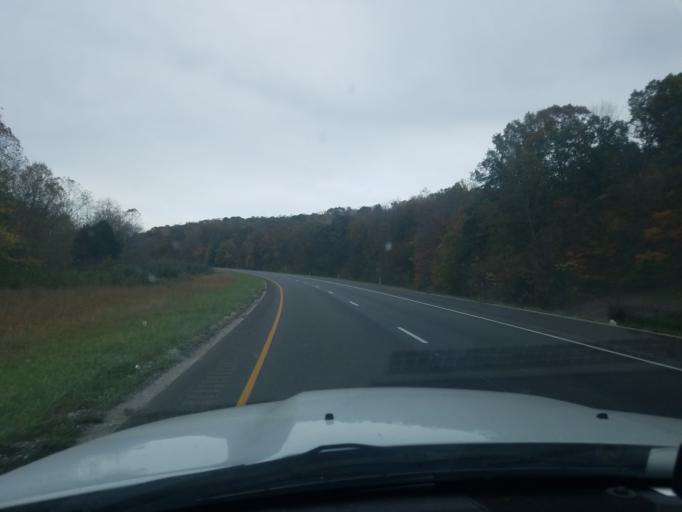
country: US
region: Indiana
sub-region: Crawford County
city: English
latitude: 38.2380
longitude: -86.4043
